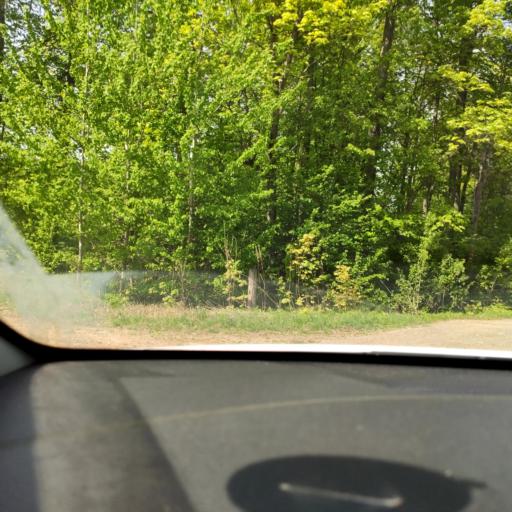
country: RU
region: Tatarstan
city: Sviyazhsk
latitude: 55.7476
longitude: 48.8067
